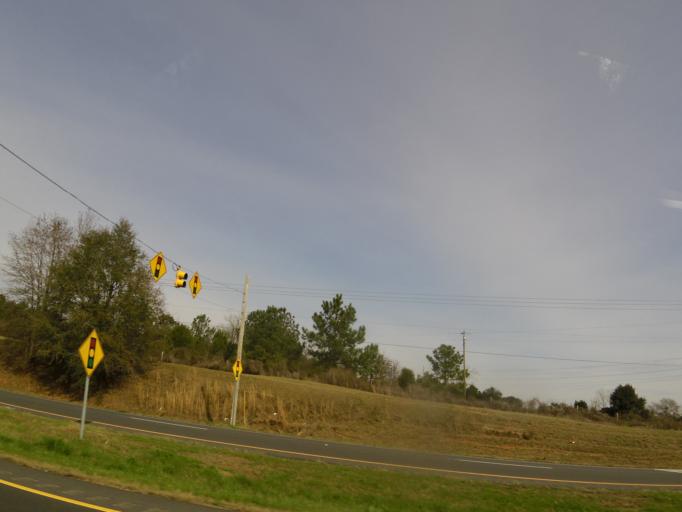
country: US
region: Alabama
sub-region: Dale County
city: Midland City
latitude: 31.2846
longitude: -85.4656
